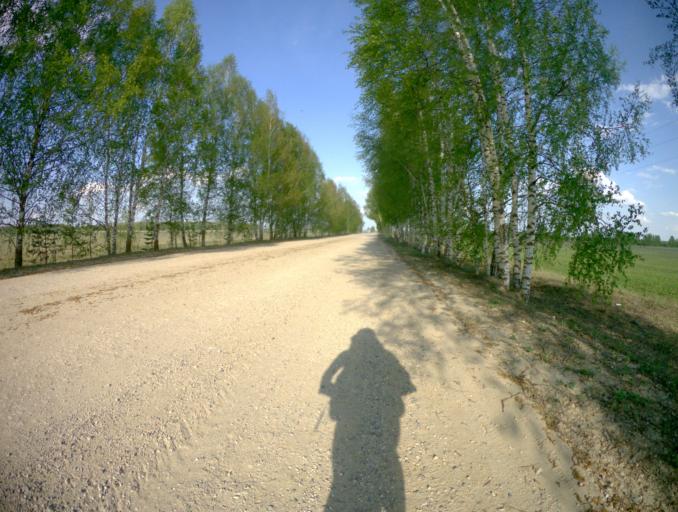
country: RU
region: Ivanovo
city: Kolobovo
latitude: 56.5405
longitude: 41.5907
